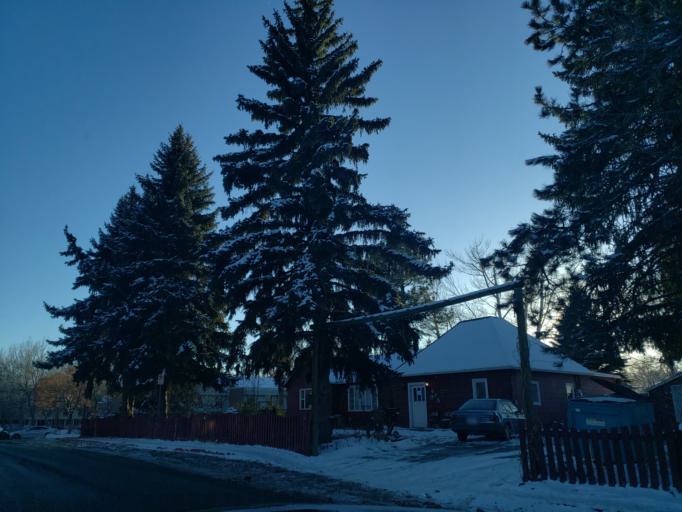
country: US
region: Colorado
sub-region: Larimer County
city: Fort Collins
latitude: 40.5791
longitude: -105.1007
